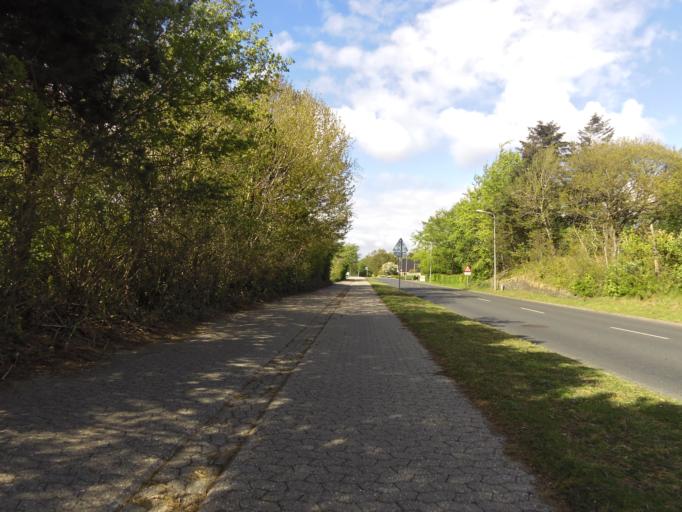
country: DK
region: South Denmark
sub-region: Esbjerg Kommune
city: Ribe
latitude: 55.2824
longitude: 8.7255
